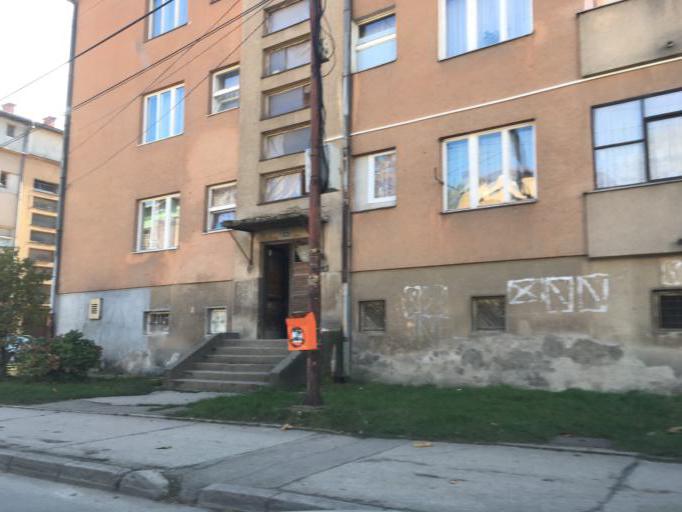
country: BA
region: Federation of Bosnia and Herzegovina
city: Novi Travnik
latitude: 44.1686
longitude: 17.6473
